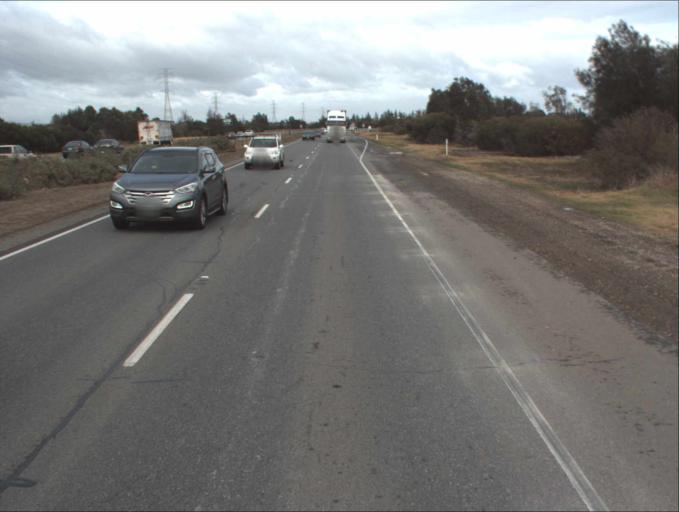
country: AU
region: South Australia
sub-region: Port Adelaide Enfield
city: Enfield
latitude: -34.8264
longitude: 138.5858
